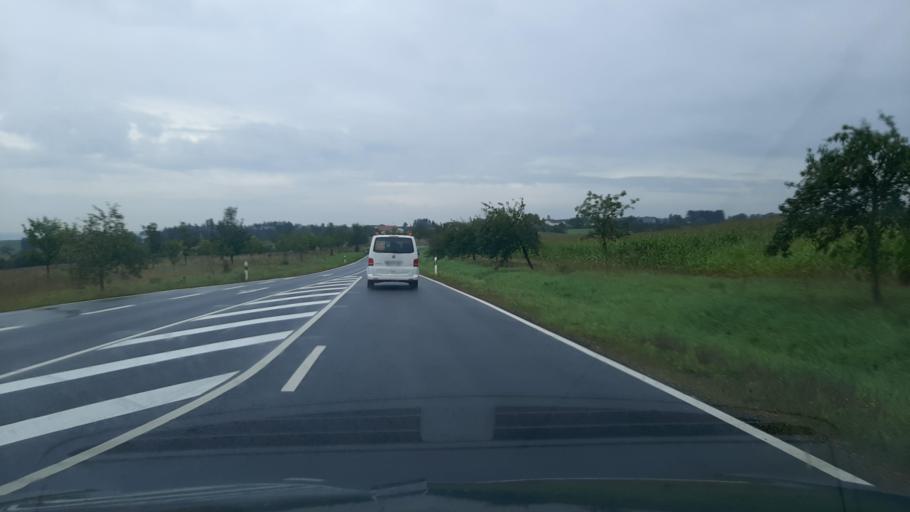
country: DE
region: Rheinland-Pfalz
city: Badem
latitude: 50.0125
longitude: 6.6095
